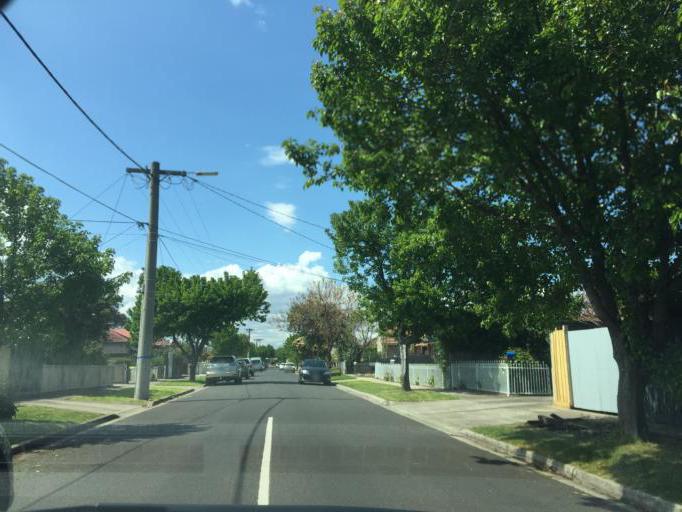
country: AU
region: Victoria
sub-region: Maribyrnong
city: West Footscray
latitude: -37.7910
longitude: 144.8675
